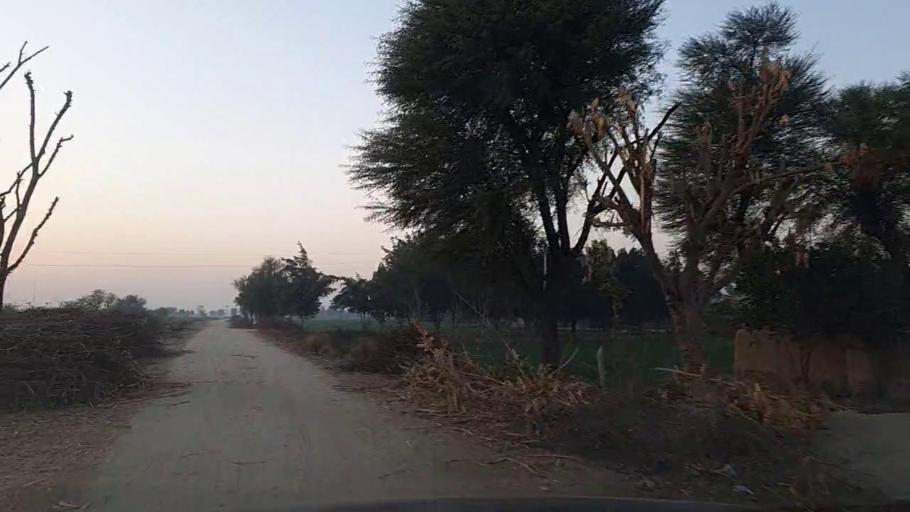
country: PK
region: Sindh
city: Daur
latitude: 26.4749
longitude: 68.5017
